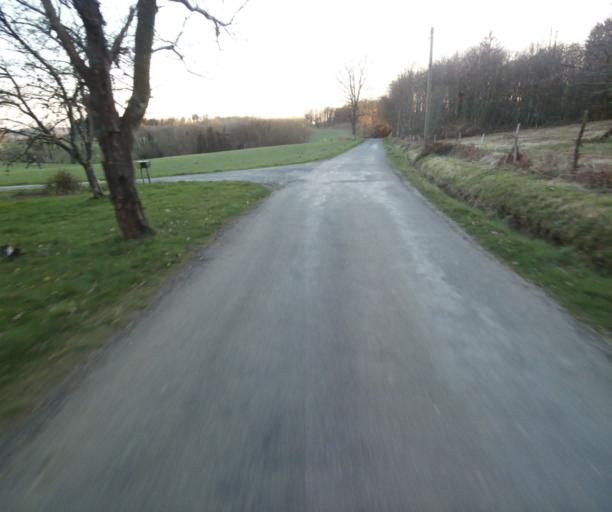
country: FR
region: Limousin
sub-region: Departement de la Correze
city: Uzerche
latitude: 45.3842
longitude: 1.6066
